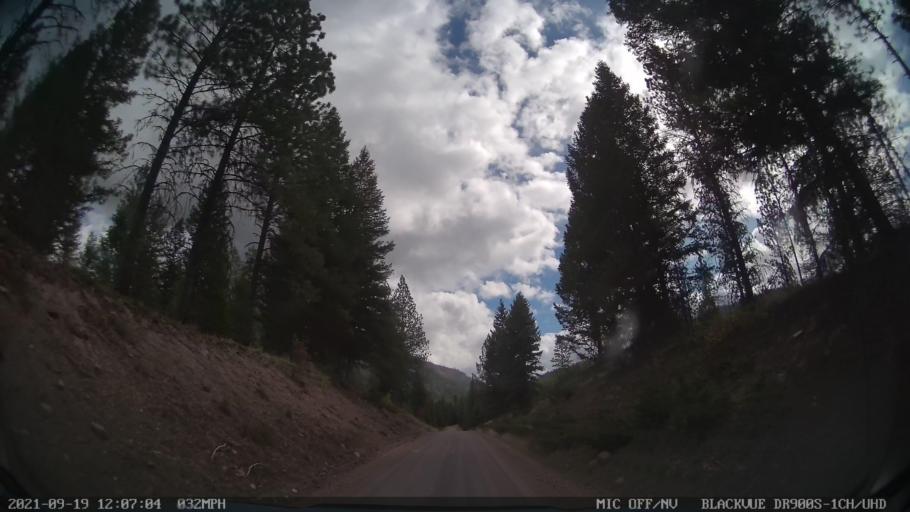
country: US
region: Montana
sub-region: Missoula County
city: Seeley Lake
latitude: 47.1846
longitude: -113.4116
